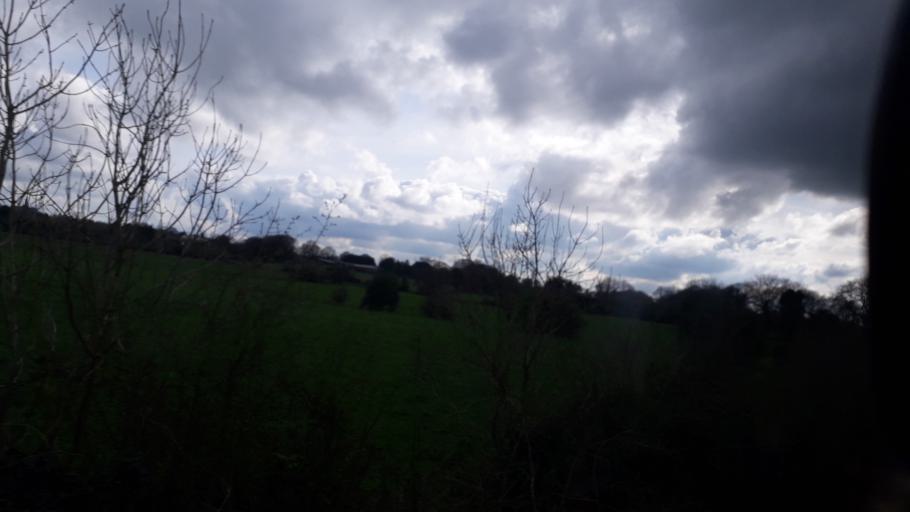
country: IE
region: Leinster
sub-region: An Iarmhi
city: Rathwire
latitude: 53.4939
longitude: -7.1909
